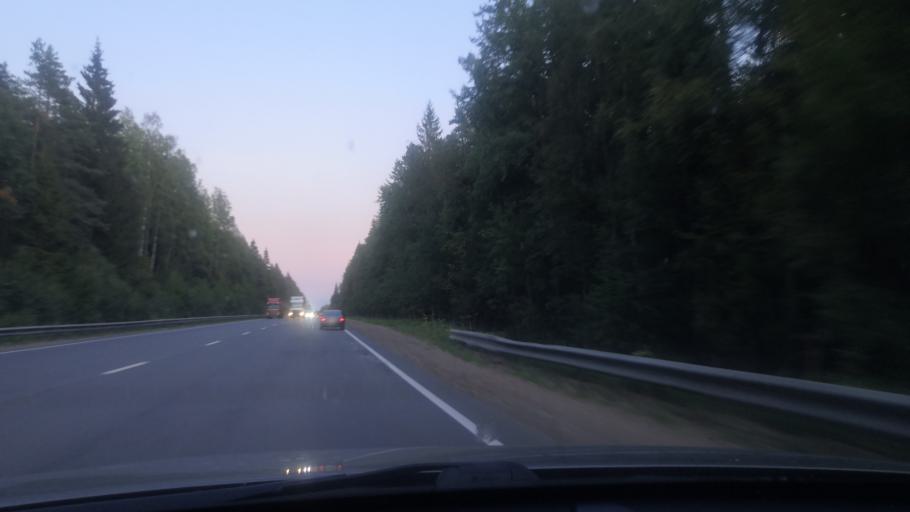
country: RU
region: St.-Petersburg
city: Pesochnyy
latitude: 60.1852
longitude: 30.1158
